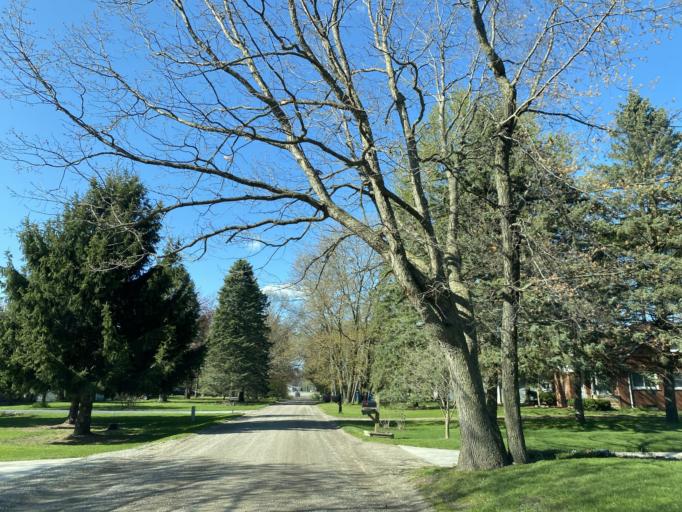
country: US
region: Michigan
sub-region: Livingston County
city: Brighton
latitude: 42.5738
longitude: -83.8421
